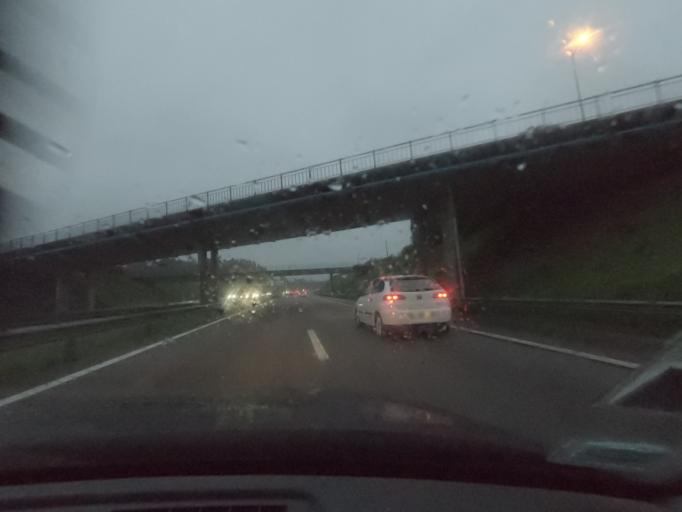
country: PT
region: Porto
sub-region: Matosinhos
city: Lavra
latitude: 41.2506
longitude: -8.6976
